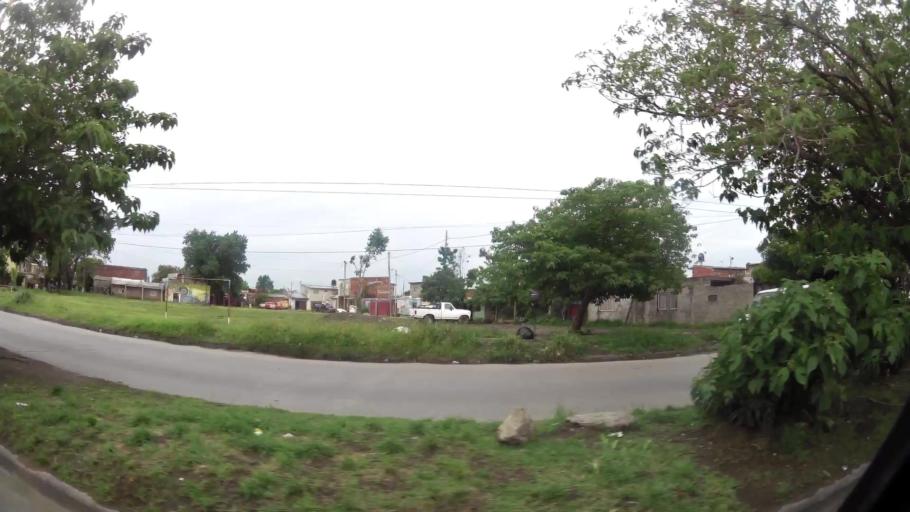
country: AR
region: Buenos Aires
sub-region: Partido de Lanus
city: Lanus
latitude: -34.7274
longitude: -58.3467
